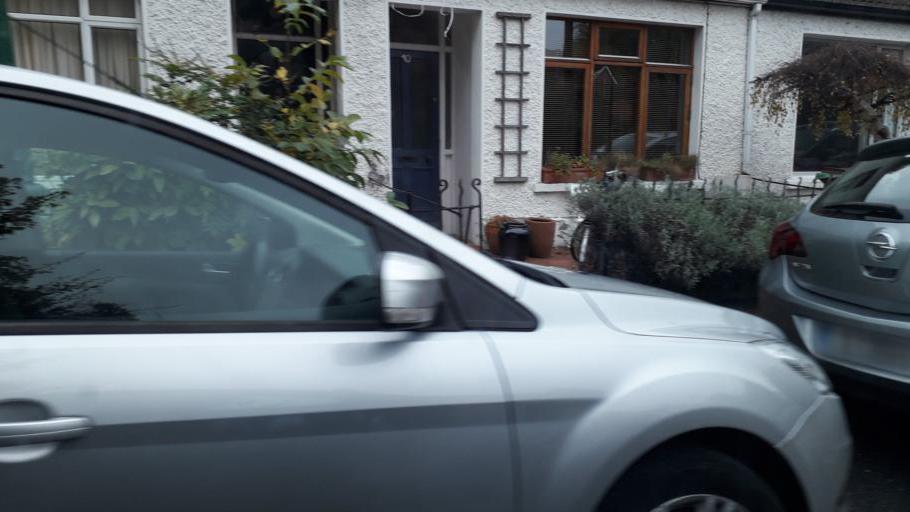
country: IE
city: Milltown
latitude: 53.3186
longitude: -6.2466
